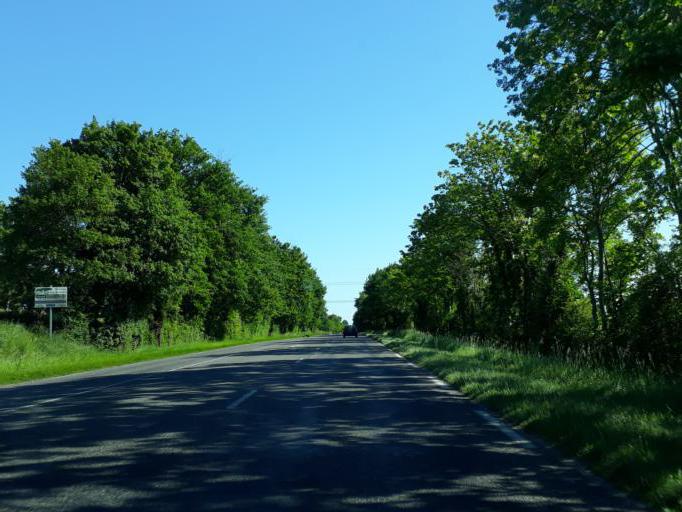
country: FR
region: Bourgogne
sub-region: Departement de la Nievre
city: Cosne-Cours-sur-Loire
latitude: 47.4639
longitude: 2.9305
